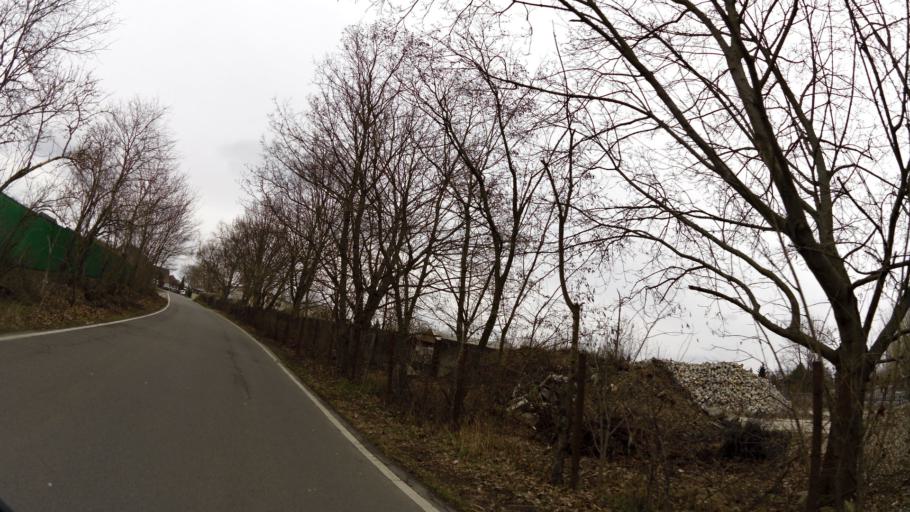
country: DE
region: Berlin
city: Bohnsdorf
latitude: 52.3973
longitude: 13.5535
